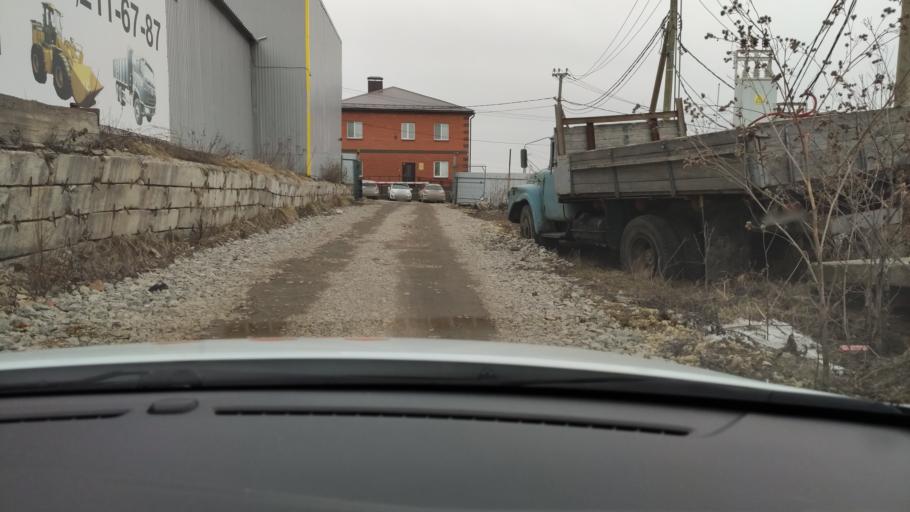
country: RU
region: Tatarstan
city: Vysokaya Gora
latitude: 55.8012
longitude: 49.2848
